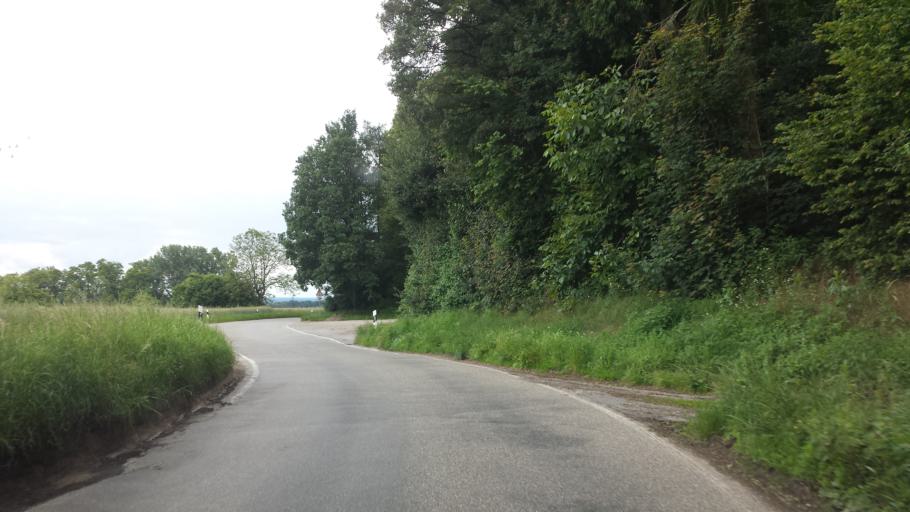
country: DE
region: Baden-Wuerttemberg
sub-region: Karlsruhe Region
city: Nussloch
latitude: 49.3235
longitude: 8.7250
